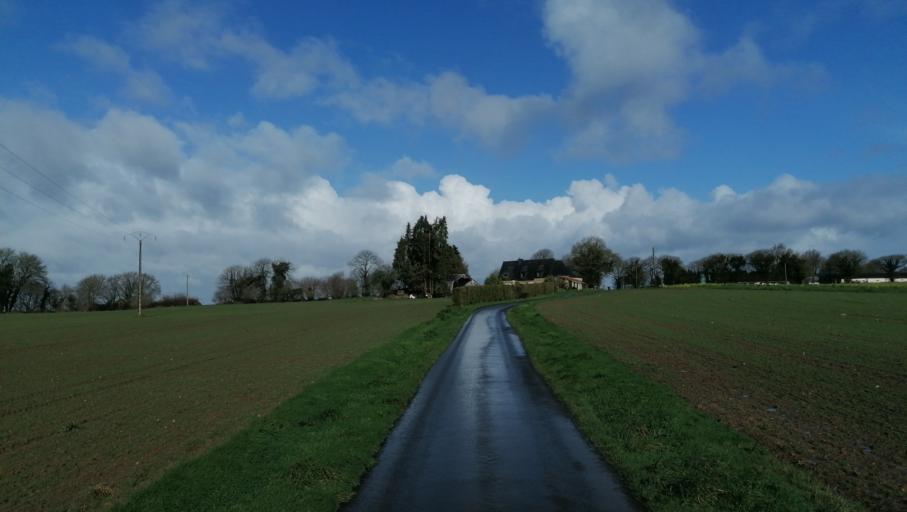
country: FR
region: Brittany
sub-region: Departement des Cotes-d'Armor
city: Lanrodec
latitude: 48.4849
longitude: -3.0203
